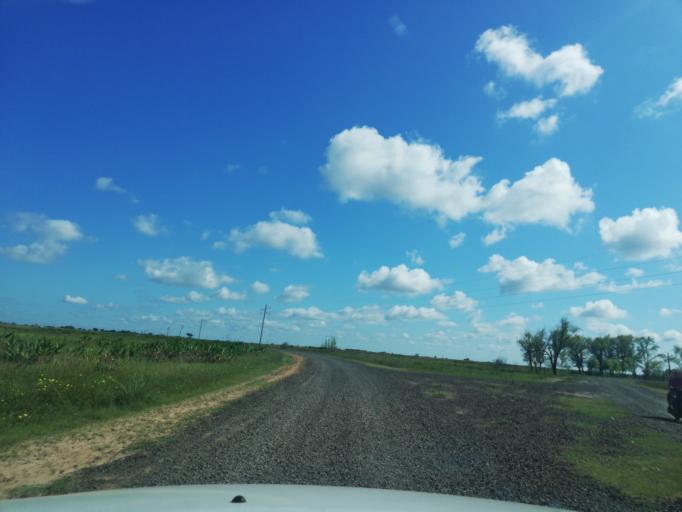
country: AR
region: Corrientes
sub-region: Departamento de San Miguel
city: San Miguel
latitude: -27.9821
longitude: -57.5810
